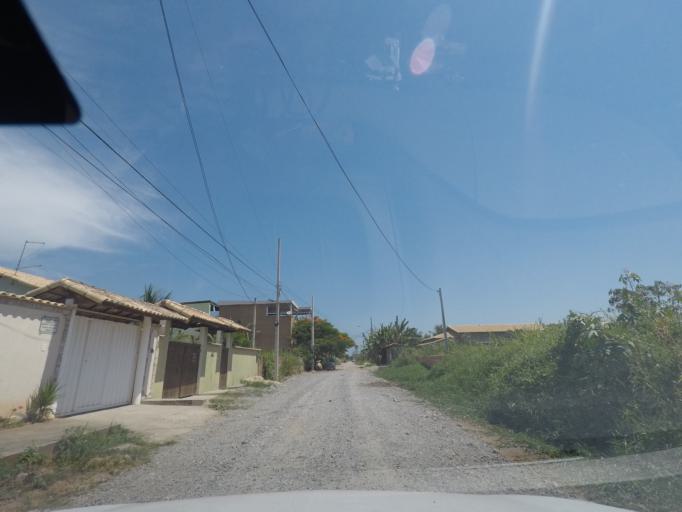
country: BR
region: Rio de Janeiro
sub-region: Marica
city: Marica
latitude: -22.9530
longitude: -42.9568
